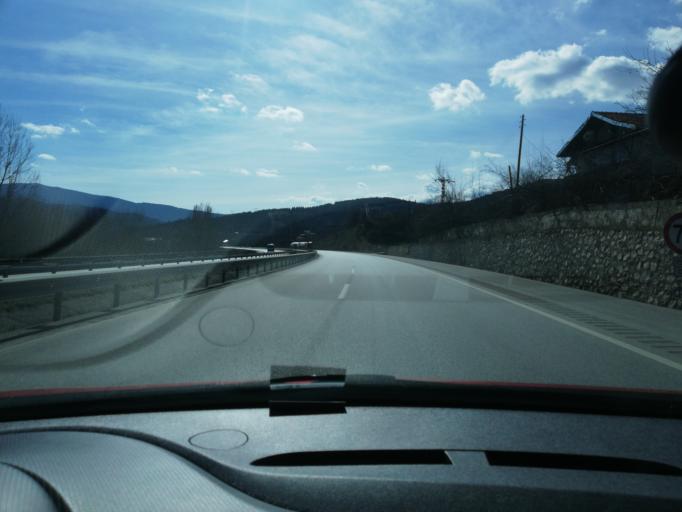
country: TR
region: Karabuk
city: Eskipazar
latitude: 41.0248
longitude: 32.6296
